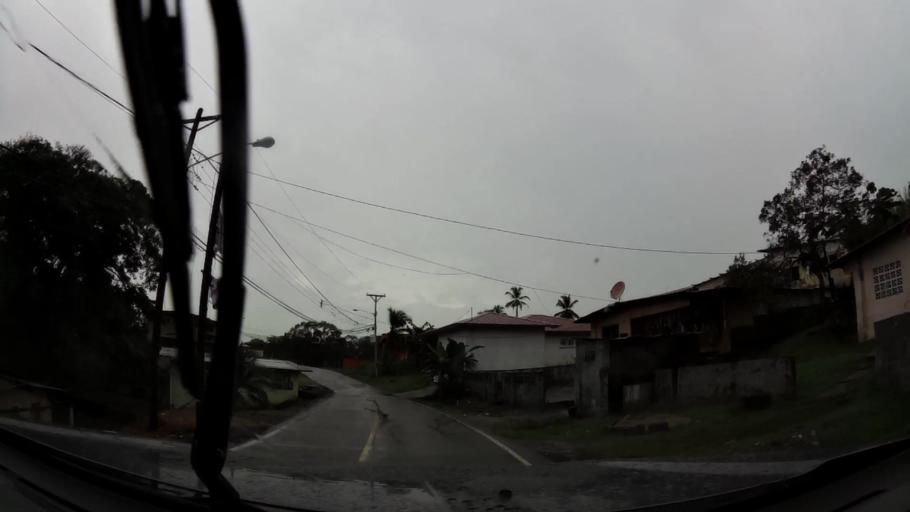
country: PA
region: Colon
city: Puerto Pilon
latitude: 9.3596
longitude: -79.8034
